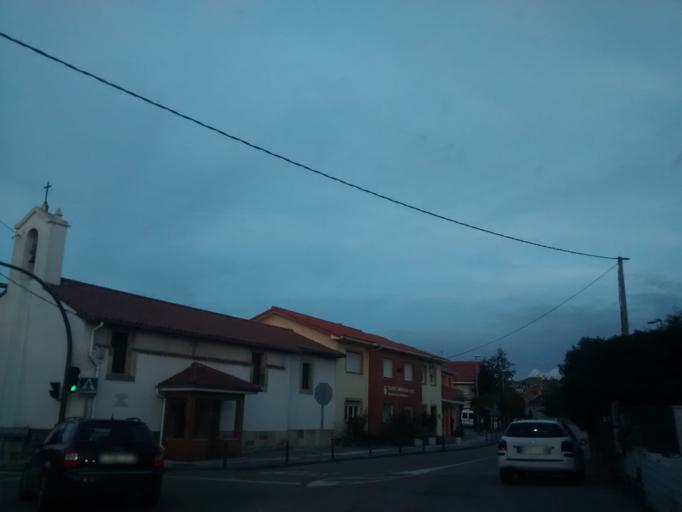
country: ES
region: Cantabria
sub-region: Provincia de Cantabria
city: Santa Cruz de Bezana
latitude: 43.4263
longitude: -3.9406
